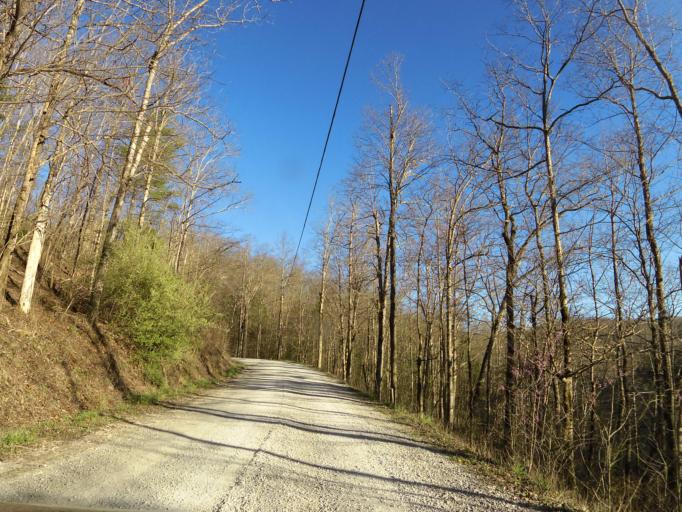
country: US
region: Tennessee
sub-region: Campbell County
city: Caryville
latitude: 36.2567
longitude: -84.3493
